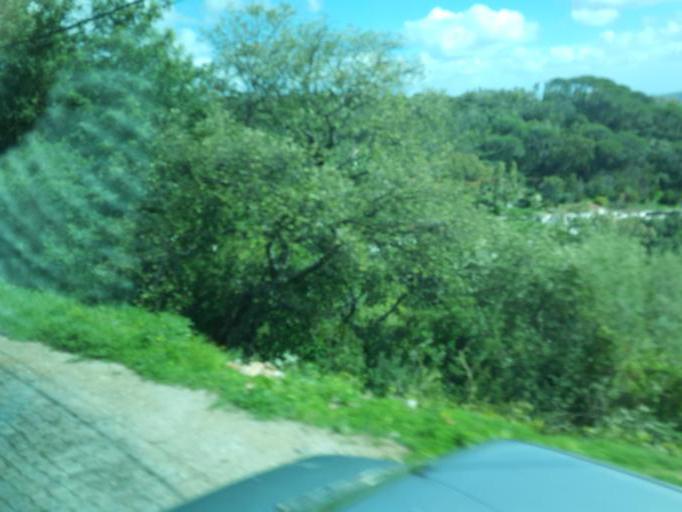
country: PT
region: Faro
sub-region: Monchique
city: Monchique
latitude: 37.2855
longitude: -8.5566
